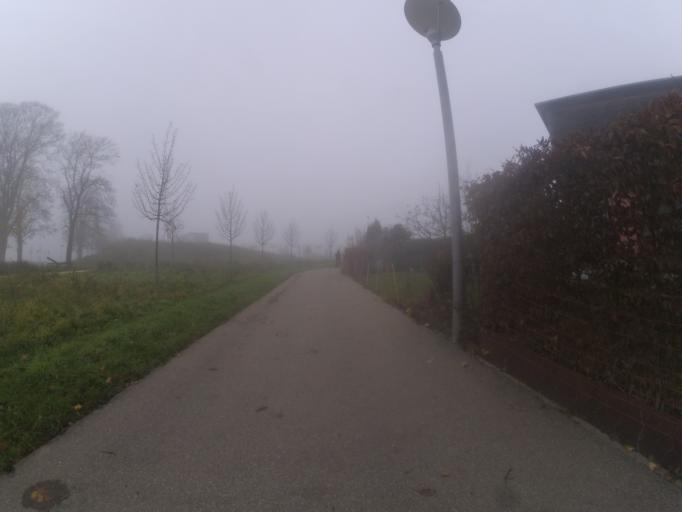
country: DE
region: Bavaria
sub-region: Swabia
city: Neu-Ulm
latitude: 48.3736
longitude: 10.0127
